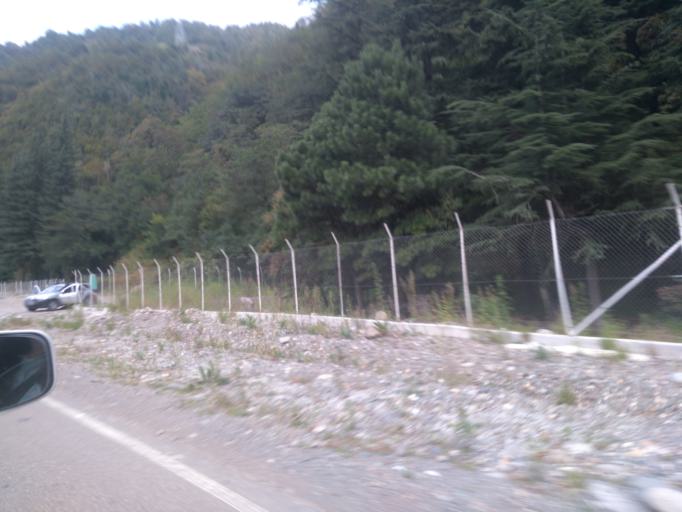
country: GE
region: Ajaria
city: Khelvachauri
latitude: 41.5473
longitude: 41.7059
